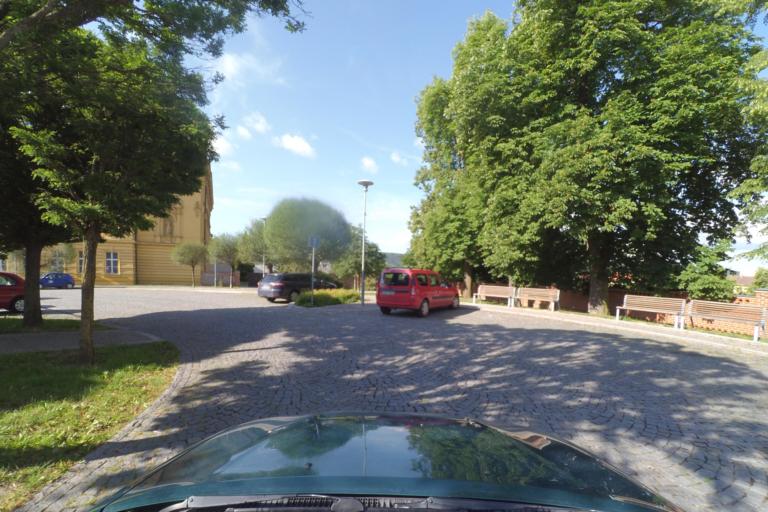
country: CZ
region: Kralovehradecky
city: Dvur Kralove nad Labem
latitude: 50.4307
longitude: 15.8119
